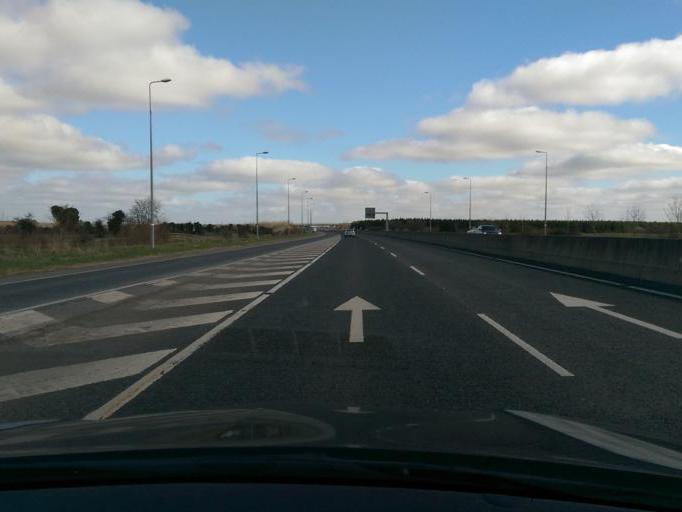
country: IE
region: Leinster
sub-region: An Iarmhi
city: Rochfortbridge
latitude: 53.4069
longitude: -7.2798
